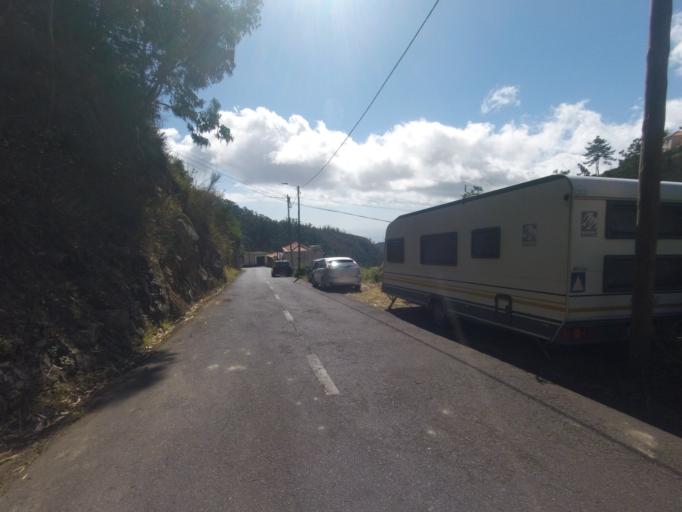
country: PT
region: Madeira
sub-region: Ribeira Brava
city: Campanario
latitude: 32.6909
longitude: -17.0310
